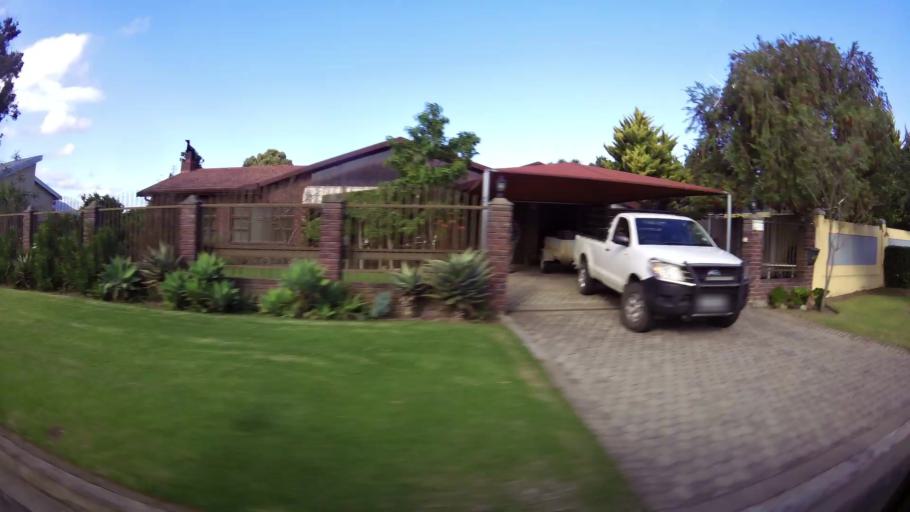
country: ZA
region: Western Cape
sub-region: Eden District Municipality
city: George
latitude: -33.9643
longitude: 22.4871
